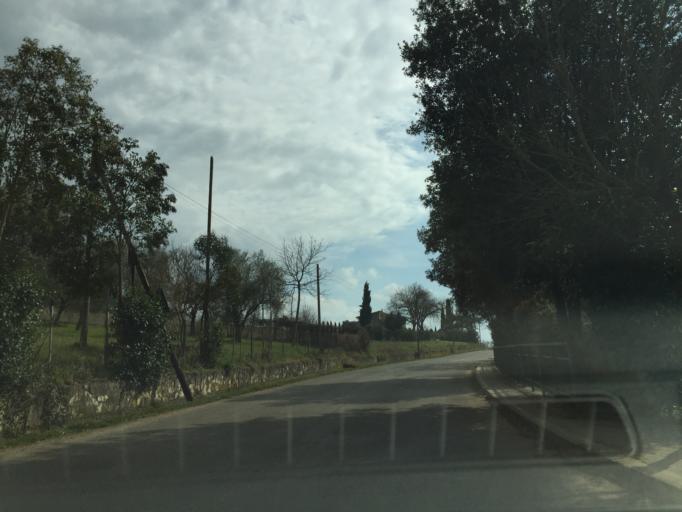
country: IT
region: Latium
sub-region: Provincia di Frosinone
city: Castrocielo
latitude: 41.5192
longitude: 13.7088
